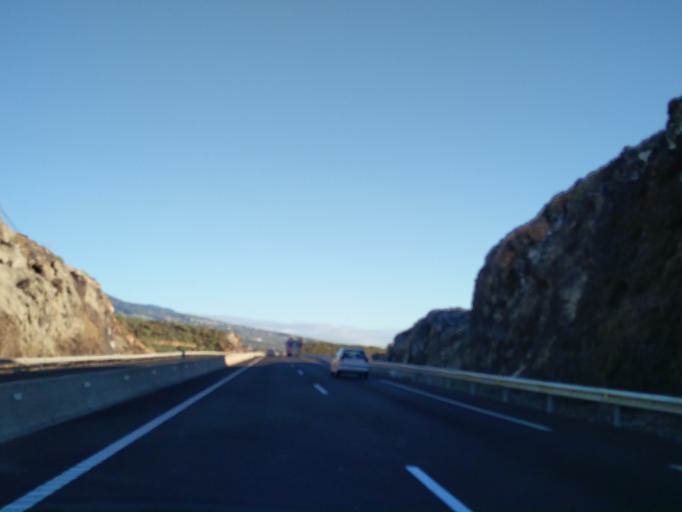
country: ES
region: Canary Islands
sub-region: Provincia de Santa Cruz de Tenerife
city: Lomo de Arico
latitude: 28.1788
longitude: -16.4306
